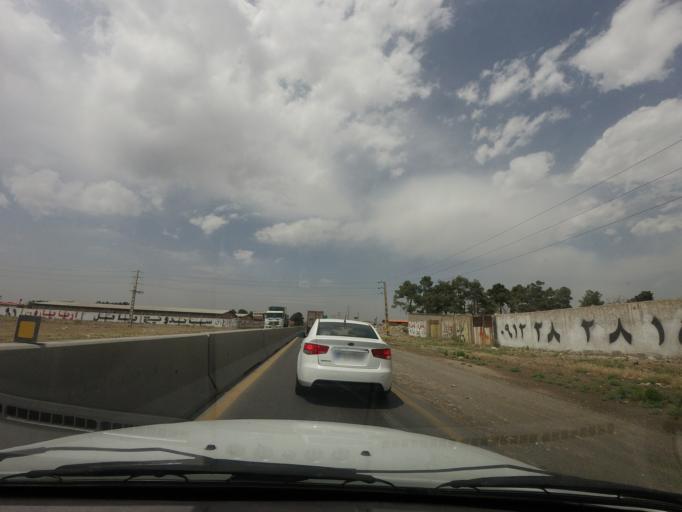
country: IR
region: Tehran
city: Shahrak-e Emam Hasan-e Mojtaba
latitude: 35.5079
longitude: 51.3066
